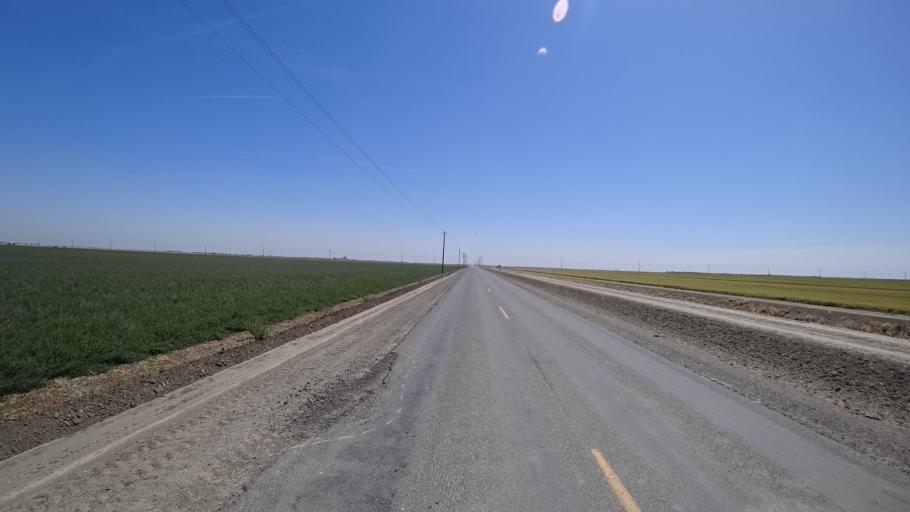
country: US
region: California
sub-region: Kings County
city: Corcoran
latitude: 36.0216
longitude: -119.5772
